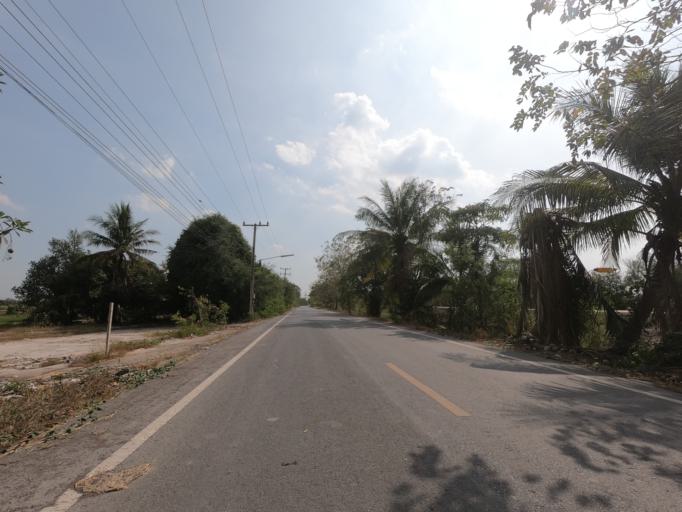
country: TH
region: Pathum Thani
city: Nong Suea
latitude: 14.1399
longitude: 100.8464
